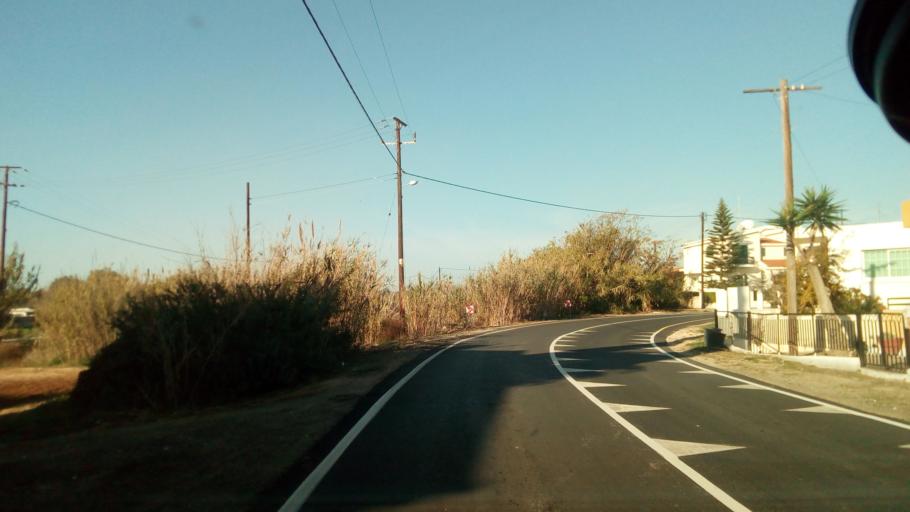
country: CY
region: Larnaka
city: Xylotymbou
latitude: 34.9979
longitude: 33.7634
